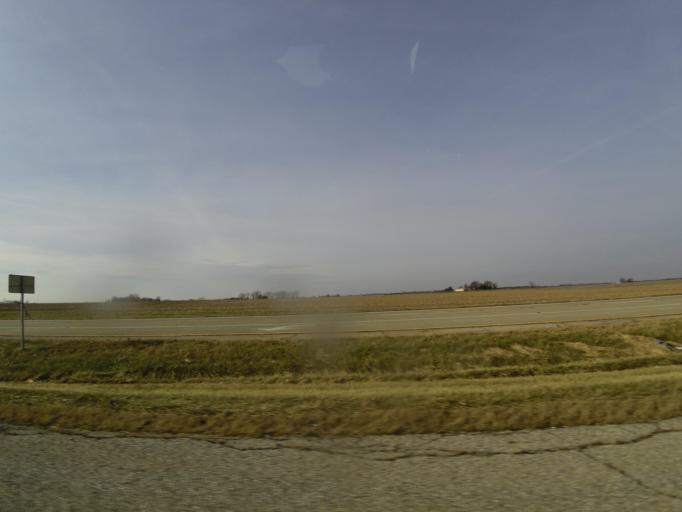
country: US
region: Illinois
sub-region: McLean County
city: Bloomington
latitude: 40.4011
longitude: -88.9897
